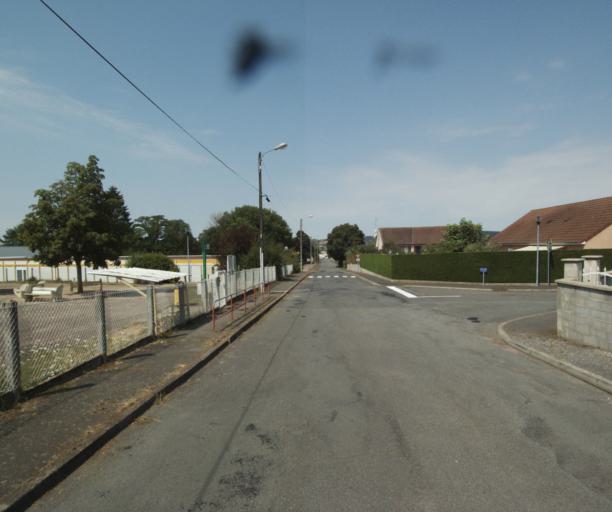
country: FR
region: Bourgogne
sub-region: Departement de Saone-et-Loire
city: Gueugnon
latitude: 46.5950
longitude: 4.0712
